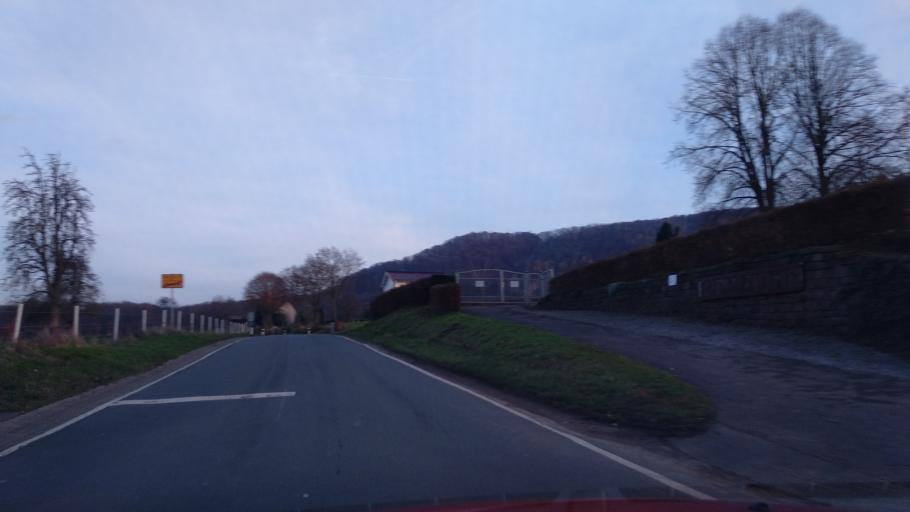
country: DE
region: North Rhine-Westphalia
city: Beverungen
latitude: 51.7116
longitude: 9.3502
